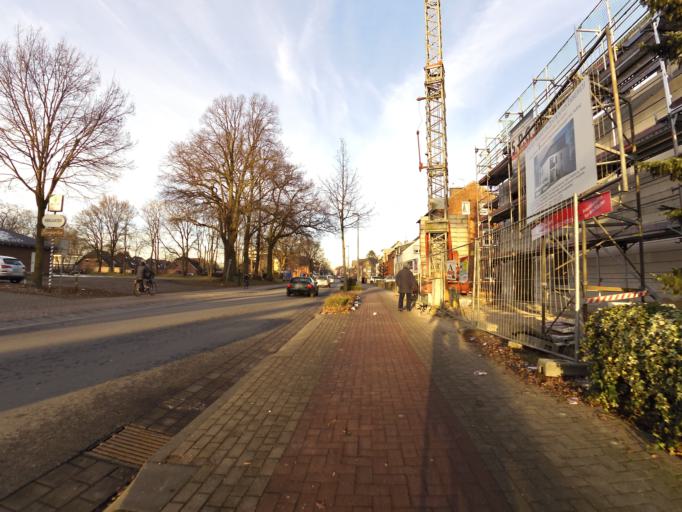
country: DE
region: North Rhine-Westphalia
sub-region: Regierungsbezirk Dusseldorf
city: Emmerich
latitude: 51.8441
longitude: 6.2532
